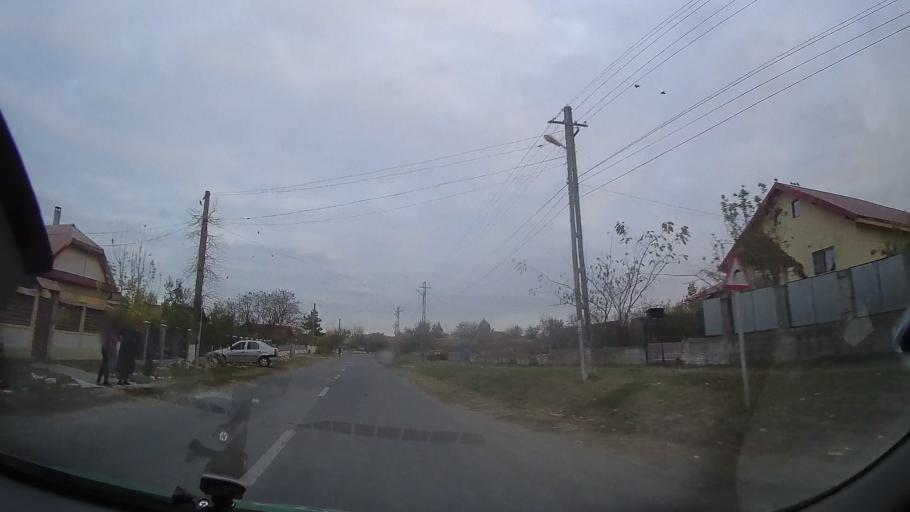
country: RO
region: Tulcea
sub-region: Comuna Mihai Bravu
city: Turda
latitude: 44.9730
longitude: 28.6256
